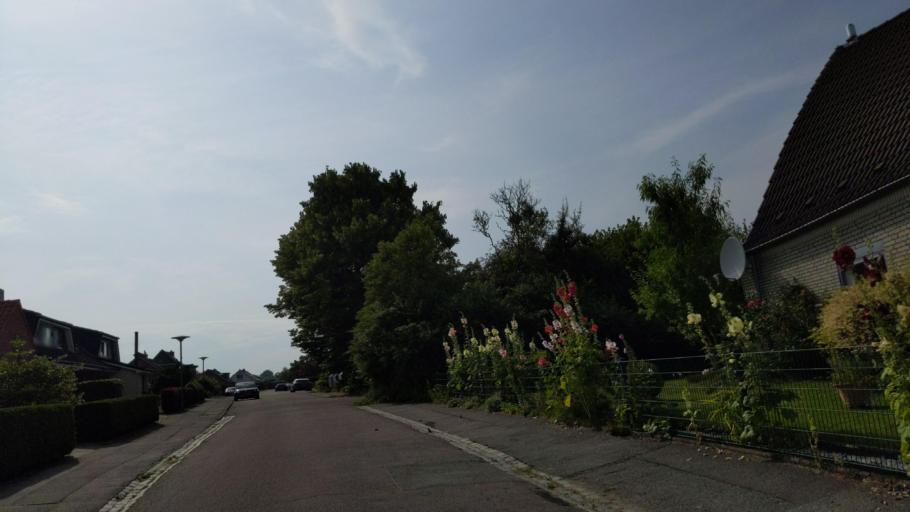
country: DE
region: Schleswig-Holstein
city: Travemuende
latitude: 53.9591
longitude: 10.8556
